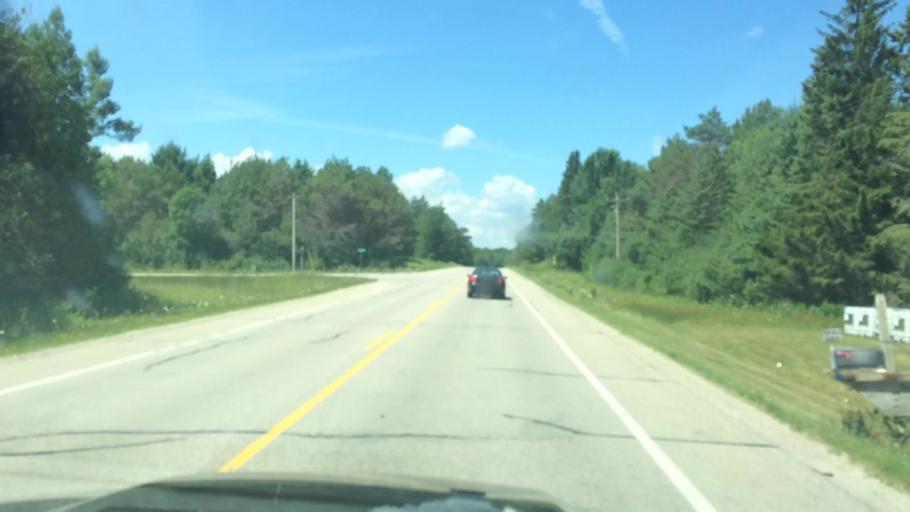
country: US
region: Wisconsin
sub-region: Marinette County
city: Peshtigo
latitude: 45.1003
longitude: -87.7325
